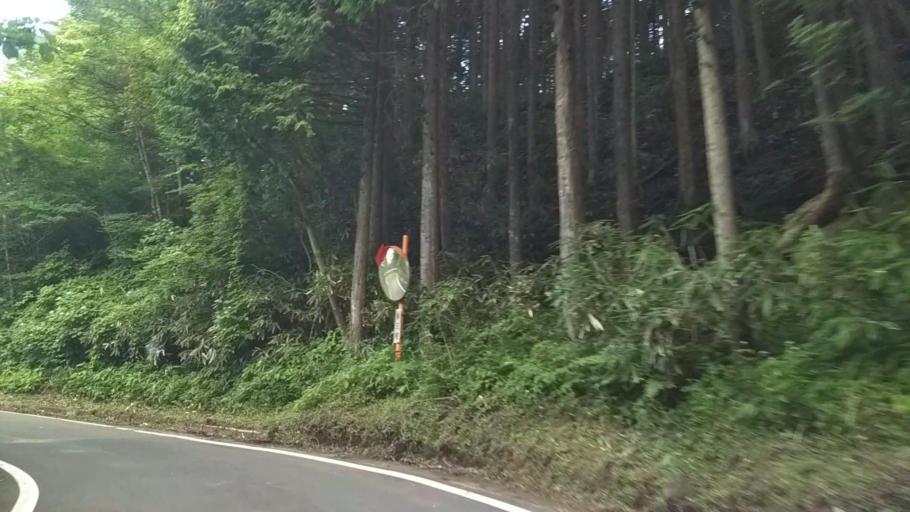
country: JP
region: Shizuoka
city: Gotemba
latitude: 35.2706
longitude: 138.9921
